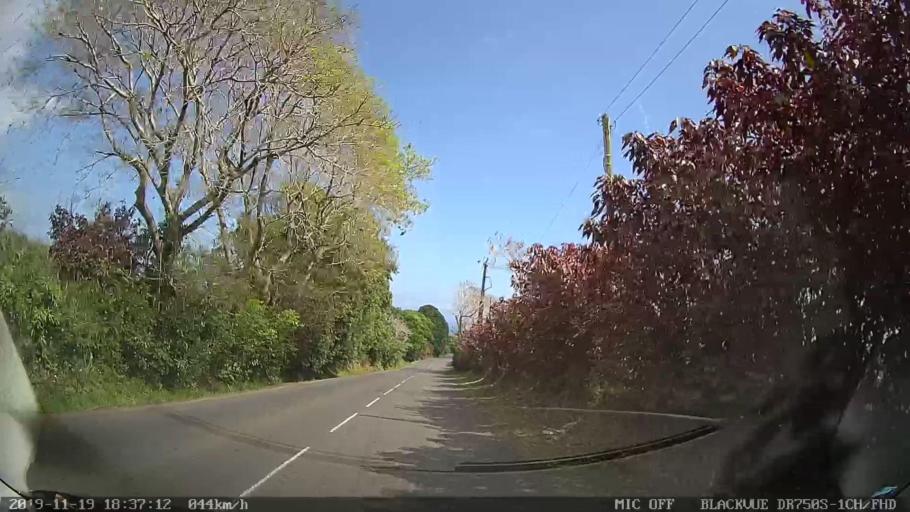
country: RE
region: Reunion
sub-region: Reunion
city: Sainte-Marie
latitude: -20.9295
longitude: 55.5308
